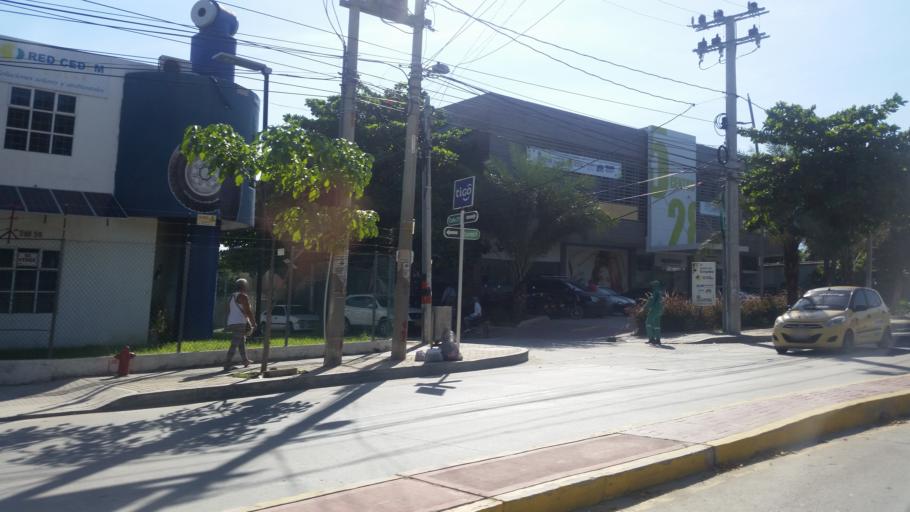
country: CO
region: Magdalena
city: Santa Marta
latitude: 11.2352
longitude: -74.2100
